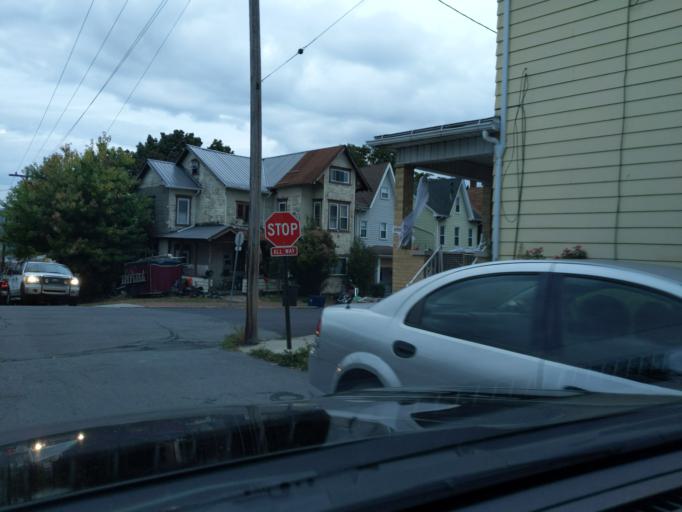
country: US
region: Pennsylvania
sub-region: Blair County
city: Altoona
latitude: 40.5122
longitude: -78.3909
